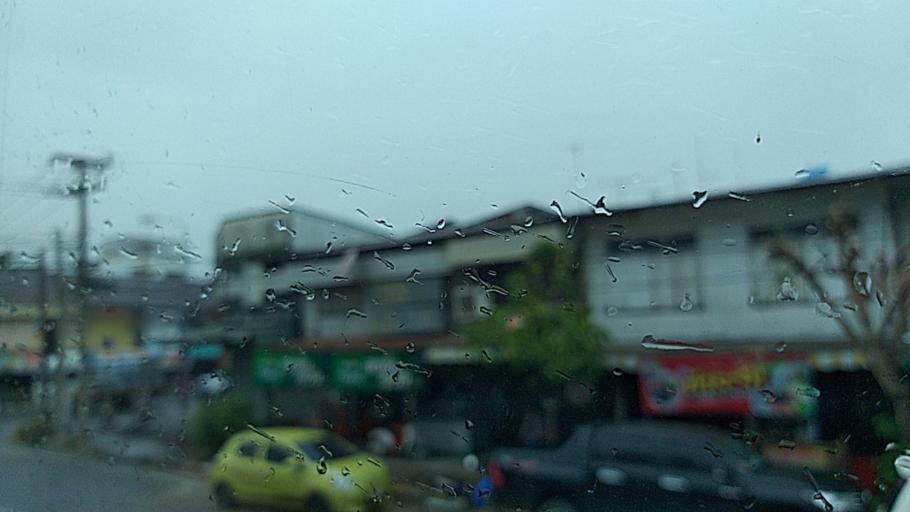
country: TH
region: Maha Sarakham
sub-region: Amphoe Borabue
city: Borabue
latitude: 16.0391
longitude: 103.1208
